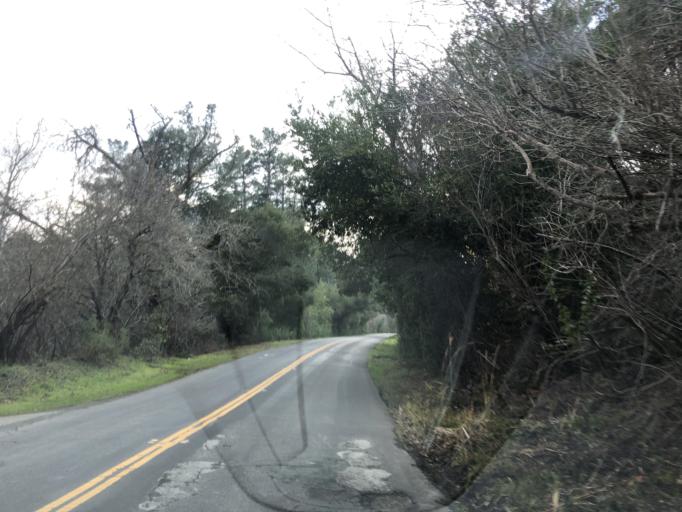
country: US
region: California
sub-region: Contra Costa County
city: Moraga
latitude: 37.8226
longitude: -122.1332
